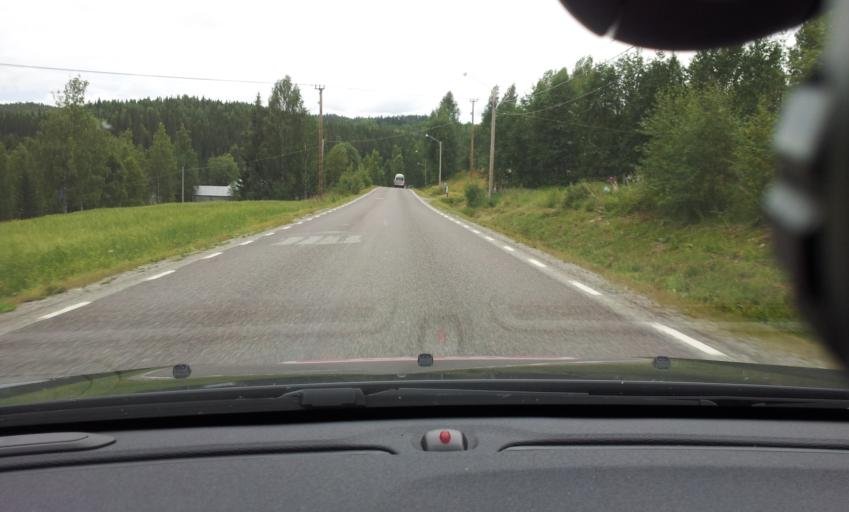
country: SE
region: Jaemtland
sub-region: Braecke Kommun
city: Braecke
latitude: 63.0368
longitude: 15.2498
